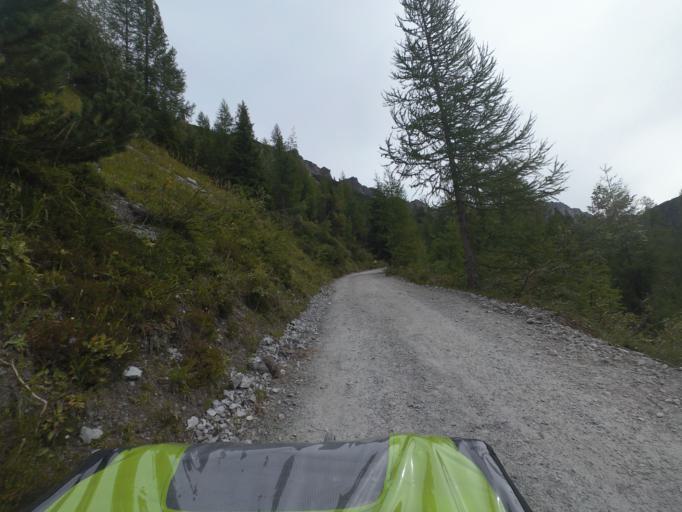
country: AT
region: Salzburg
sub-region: Politischer Bezirk Sankt Johann im Pongau
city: Untertauern
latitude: 47.2926
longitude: 13.5871
